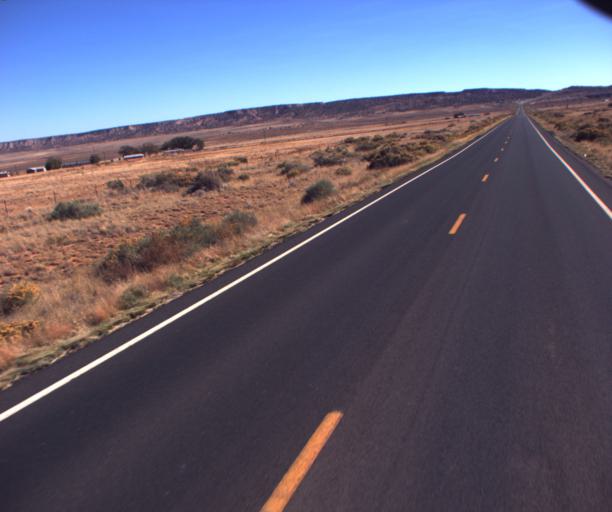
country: US
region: Arizona
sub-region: Apache County
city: Ganado
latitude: 35.7728
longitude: -109.6501
